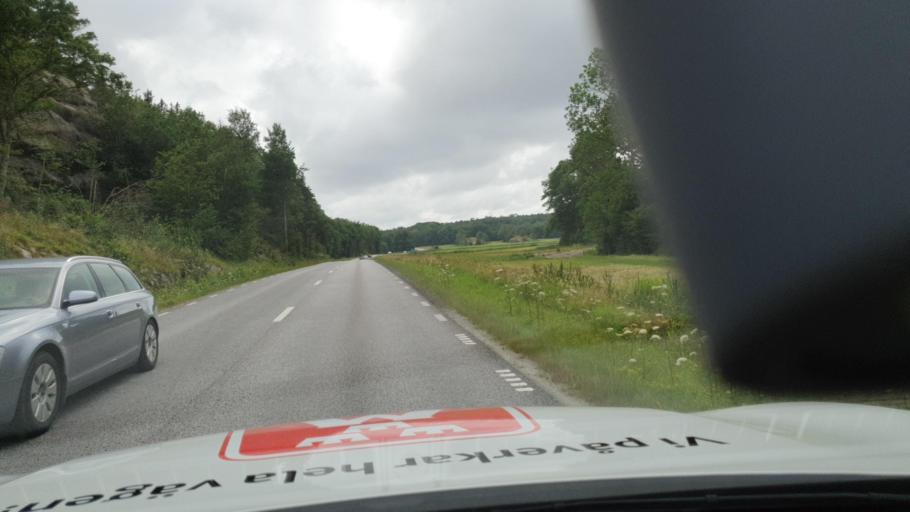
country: SE
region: Vaestra Goetaland
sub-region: Tanums Kommun
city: Grebbestad
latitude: 58.7199
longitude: 11.2750
